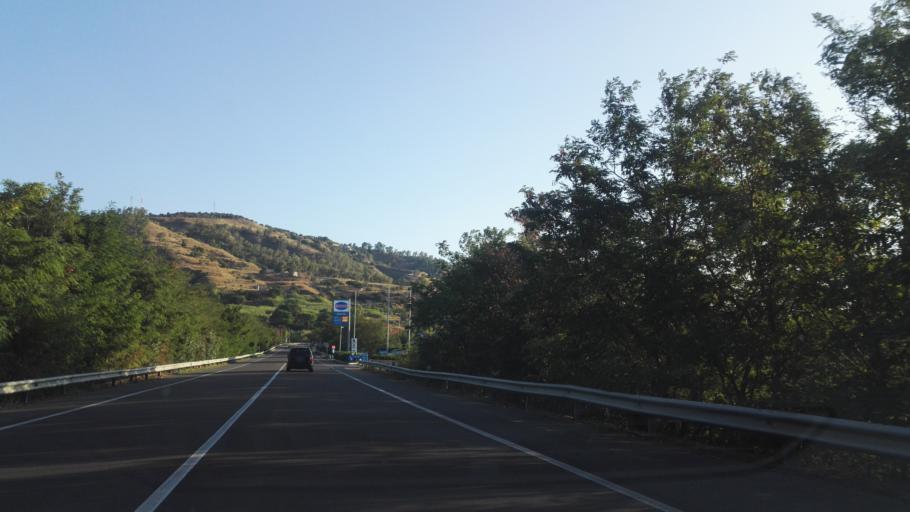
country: IT
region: Calabria
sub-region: Provincia di Catanzaro
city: Montepaone Lido
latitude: 38.7388
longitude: 16.5465
